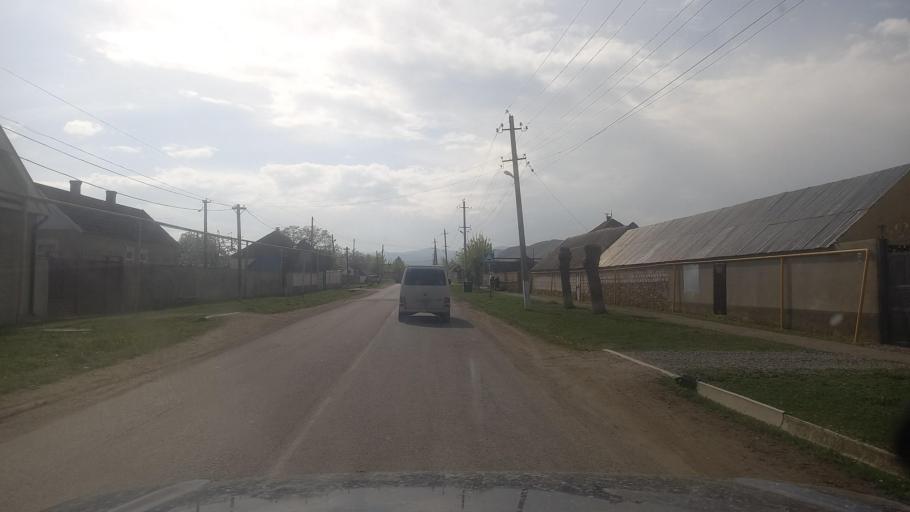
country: RU
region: Kabardino-Balkariya
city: Kamennomostskoye
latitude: 43.7350
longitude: 43.0390
